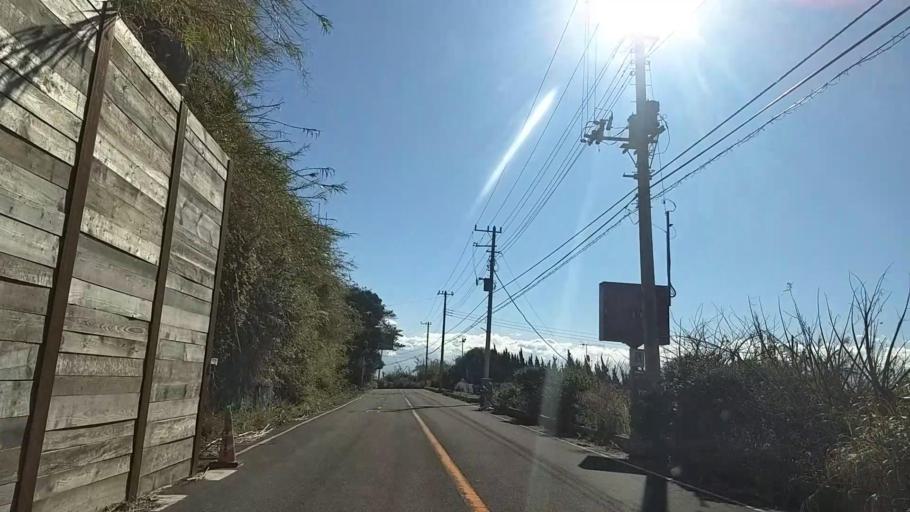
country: JP
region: Chiba
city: Tateyama
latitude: 34.9099
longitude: 139.8300
